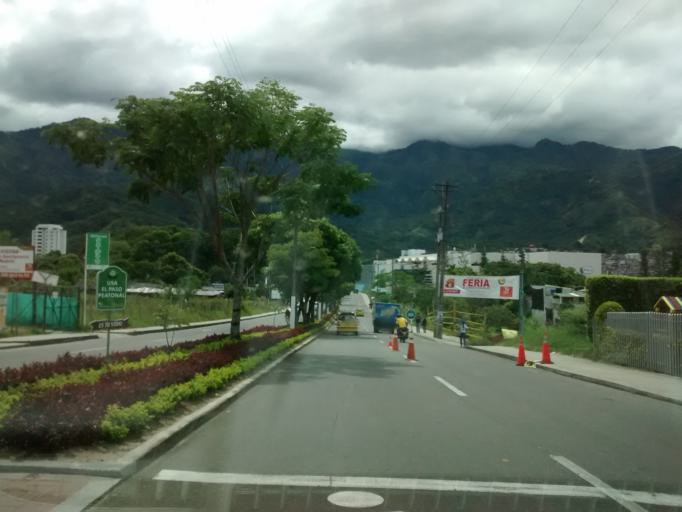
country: CO
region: Tolima
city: Ibague
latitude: 4.4421
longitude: -75.2045
